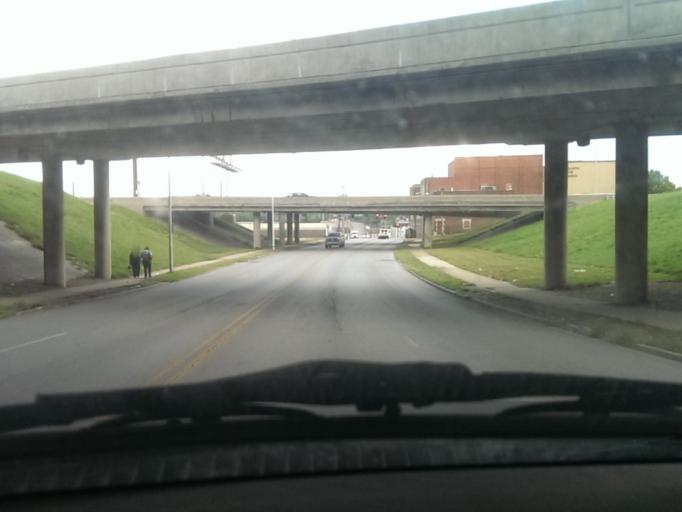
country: US
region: Missouri
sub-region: Jackson County
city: Kansas City
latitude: 39.0970
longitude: -94.5699
